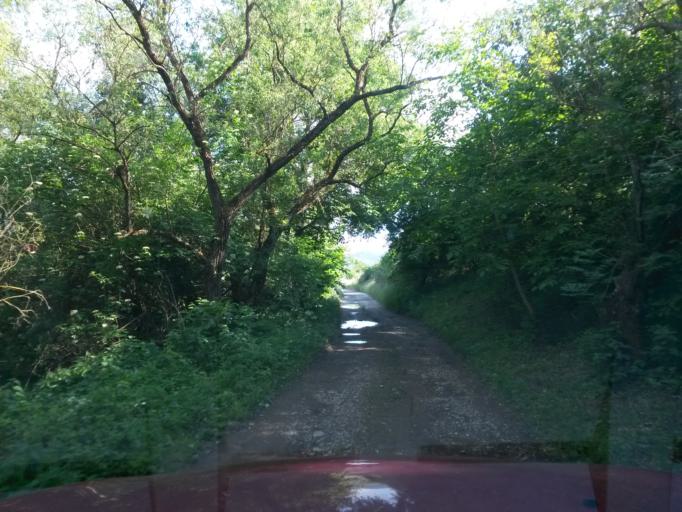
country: SK
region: Kosicky
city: Roznava
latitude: 48.5897
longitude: 20.6441
